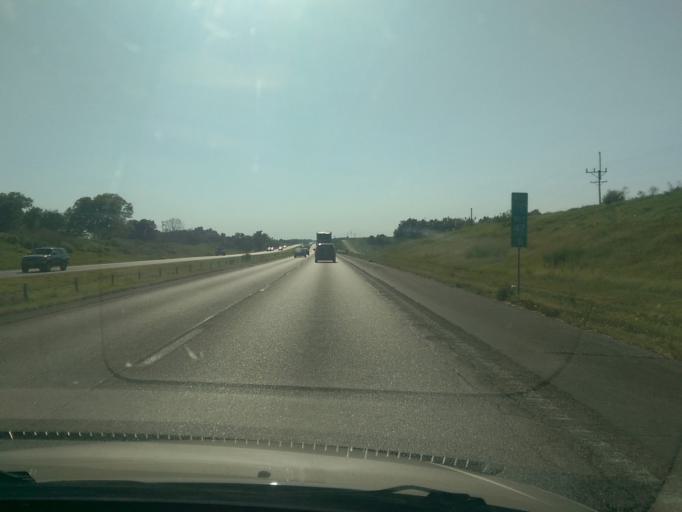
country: US
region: Missouri
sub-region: Lafayette County
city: Higginsville
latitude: 39.0019
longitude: -93.7650
